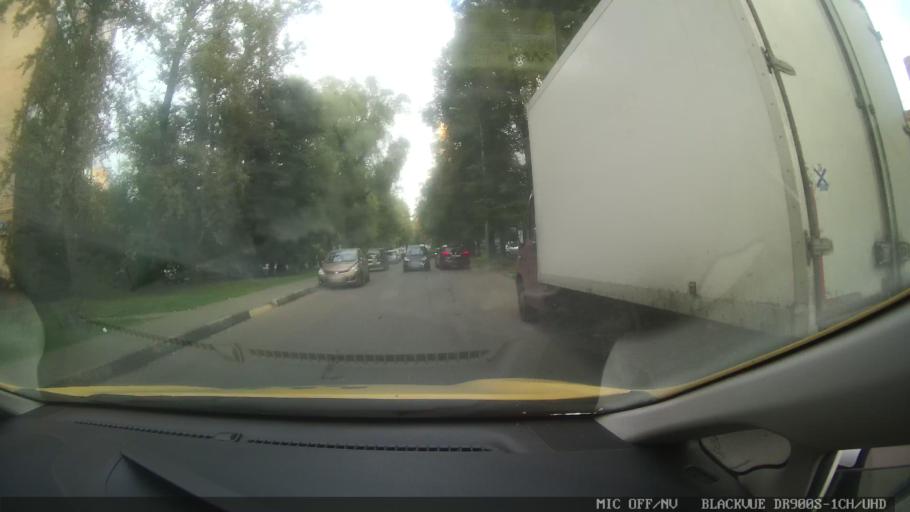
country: RU
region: Moscow
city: Vatutino
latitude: 55.8585
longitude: 37.6967
